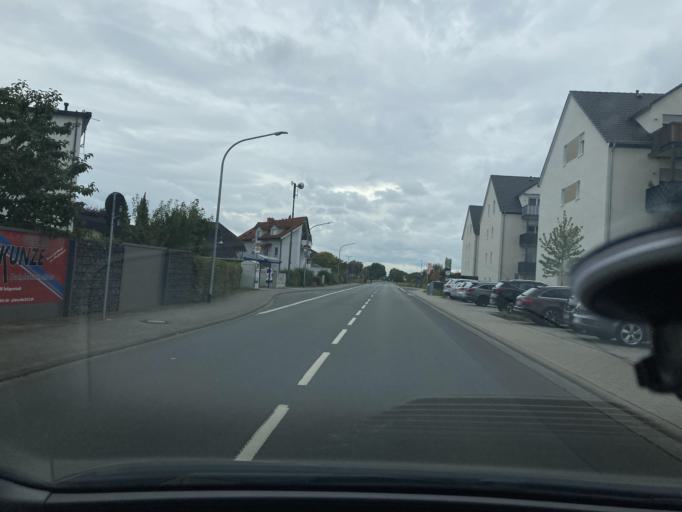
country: DE
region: Bavaria
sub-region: Regierungsbezirk Unterfranken
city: Kahl am Main
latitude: 50.0352
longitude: 9.0254
